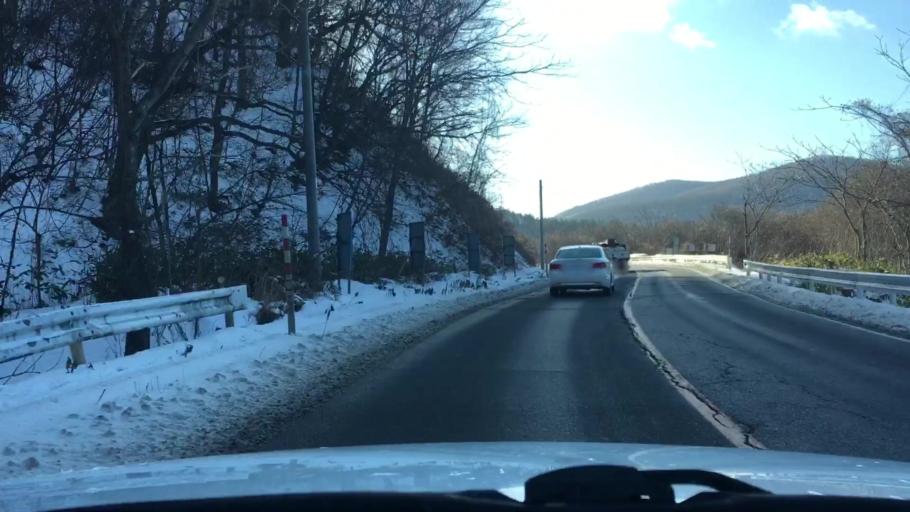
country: JP
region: Iwate
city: Morioka-shi
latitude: 39.6599
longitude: 141.3373
